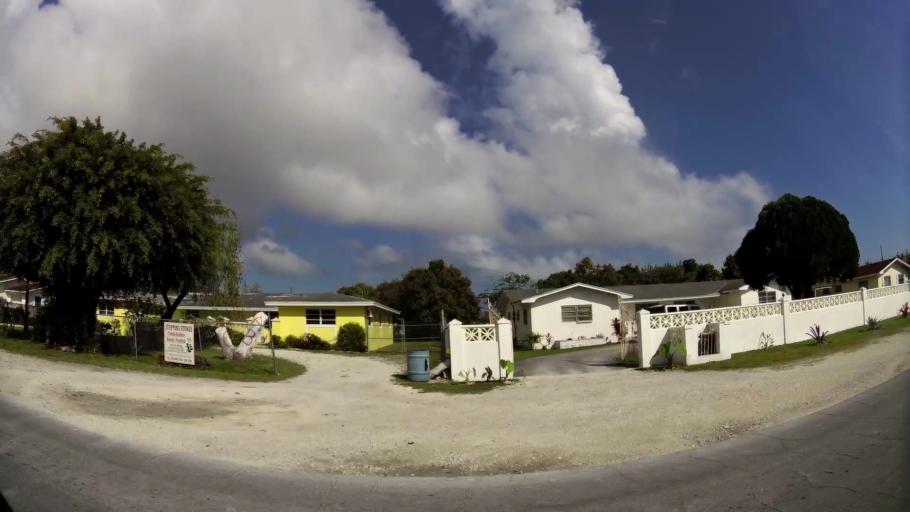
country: BS
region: Freeport
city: Freeport
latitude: 26.5204
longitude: -78.6870
